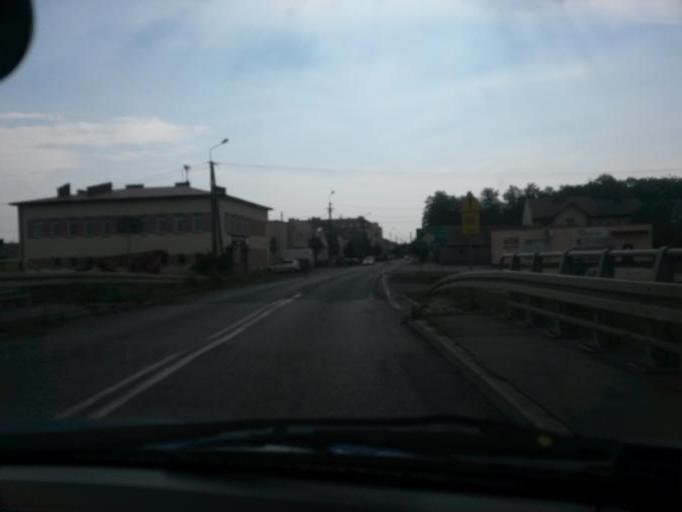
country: PL
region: Masovian Voivodeship
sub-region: Powiat zurominski
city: Biezun
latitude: 52.9627
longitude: 19.8928
